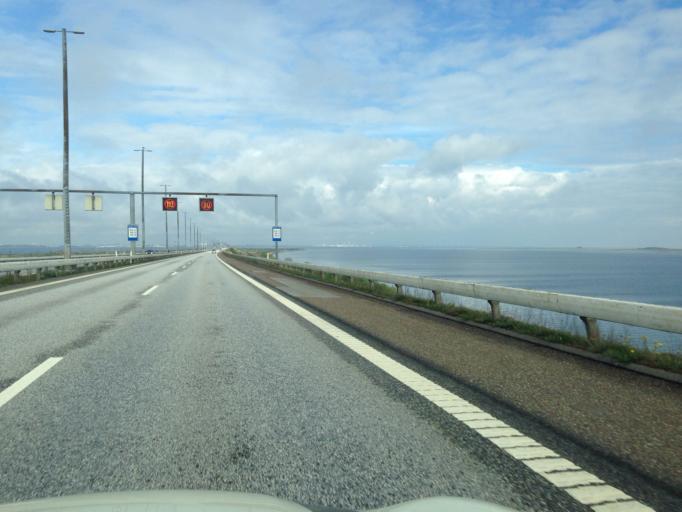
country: DK
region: Capital Region
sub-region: Dragor Kommune
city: Dragor
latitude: 55.5928
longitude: 12.7677
